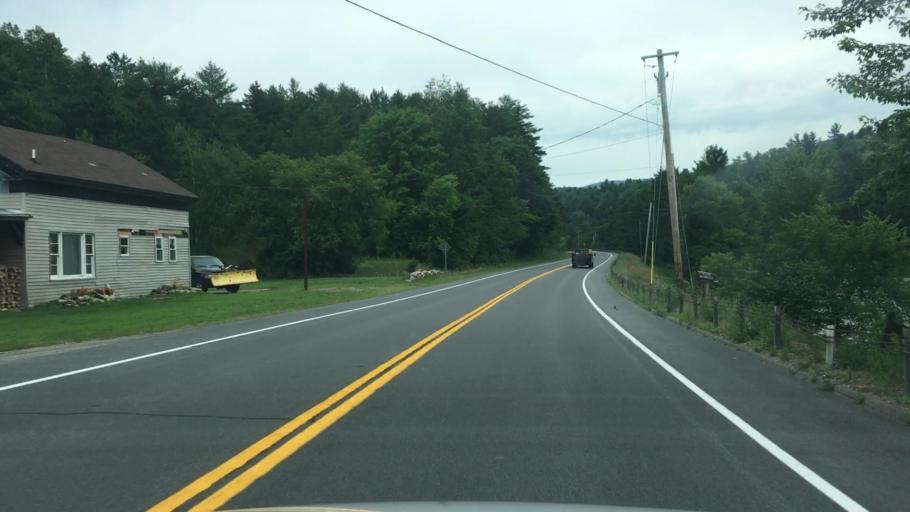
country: US
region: New York
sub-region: Essex County
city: Keeseville
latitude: 44.4577
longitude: -73.6228
